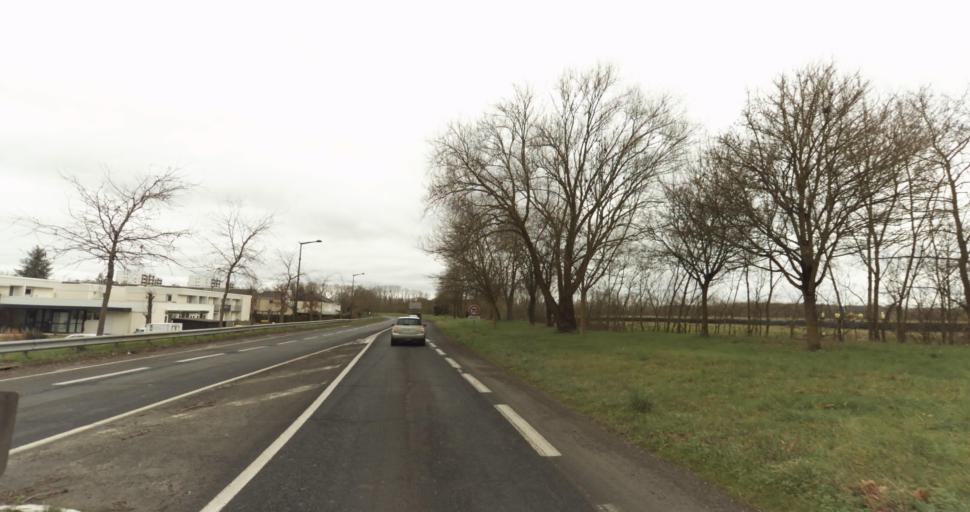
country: FR
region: Pays de la Loire
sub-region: Departement de Maine-et-Loire
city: Saumur
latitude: 47.2420
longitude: -0.0796
